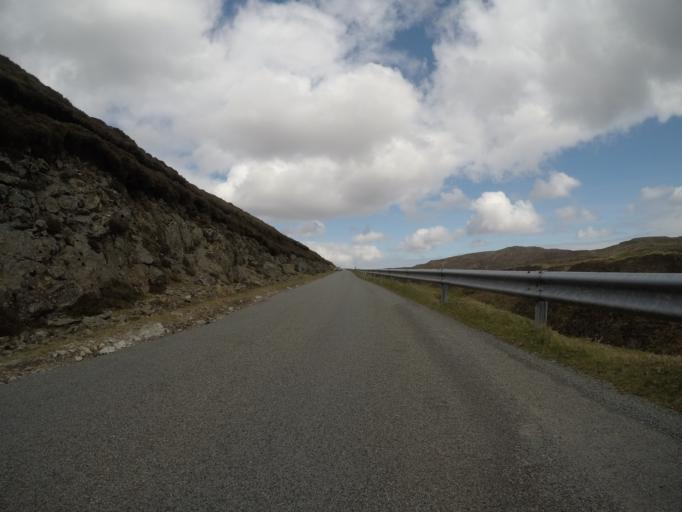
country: GB
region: Scotland
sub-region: Highland
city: Isle of Skye
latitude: 57.3774
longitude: -6.3683
